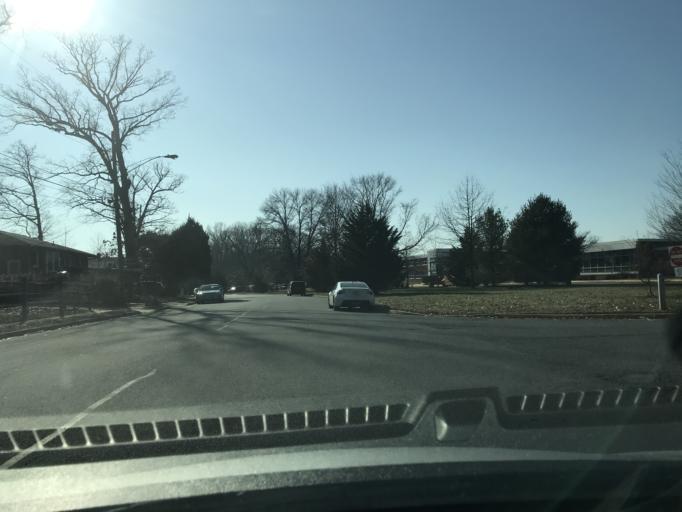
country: US
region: Virginia
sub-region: City of Fairfax
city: Fairfax
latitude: 38.8606
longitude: -77.3257
